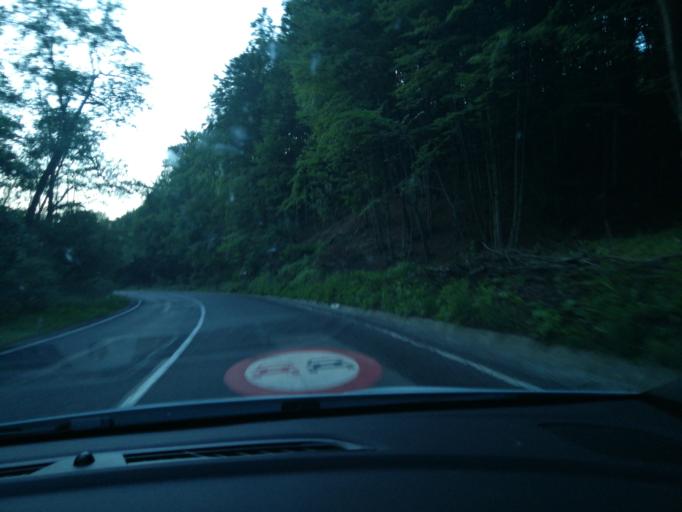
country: RO
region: Brasov
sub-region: Comuna Hoghiz
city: Hoghiz
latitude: 45.9379
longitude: 25.3869
